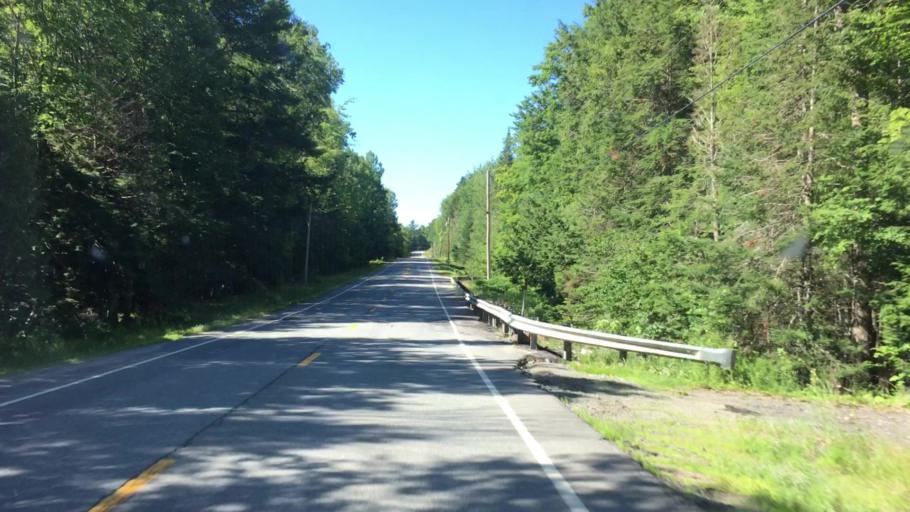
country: US
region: Maine
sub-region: Hancock County
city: Dedham
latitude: 44.6824
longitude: -68.6666
